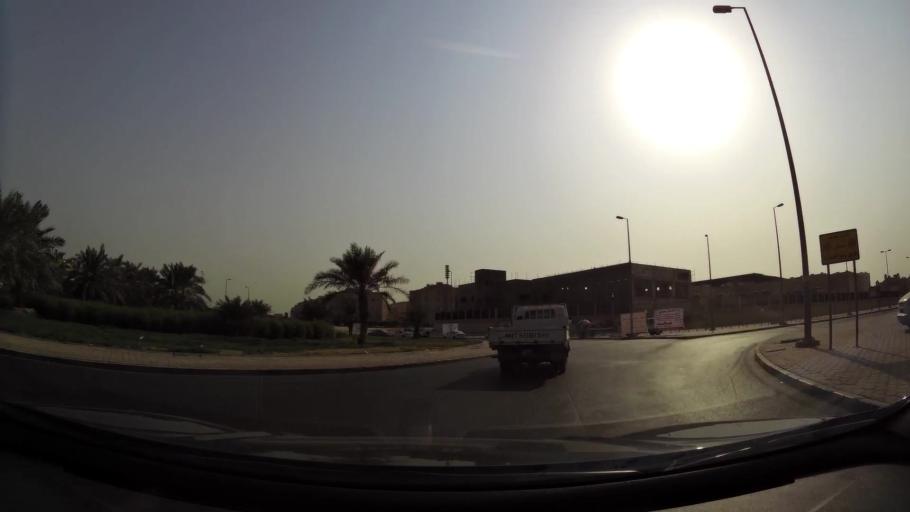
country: KW
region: Al Ahmadi
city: Ar Riqqah
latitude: 29.1276
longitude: 48.1040
